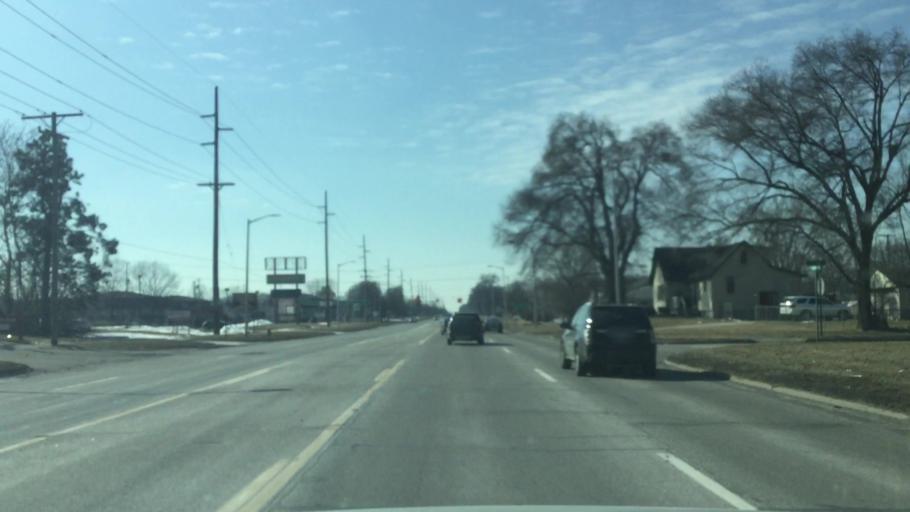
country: US
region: Michigan
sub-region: Wayne County
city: Garden City
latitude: 42.3111
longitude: -83.3373
